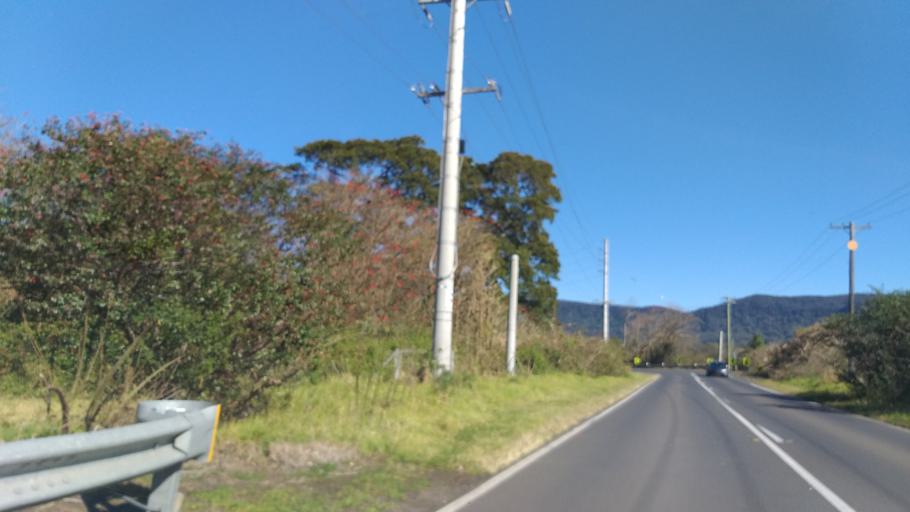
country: AU
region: New South Wales
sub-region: Wollongong
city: Dapto
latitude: -34.4691
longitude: 150.7974
